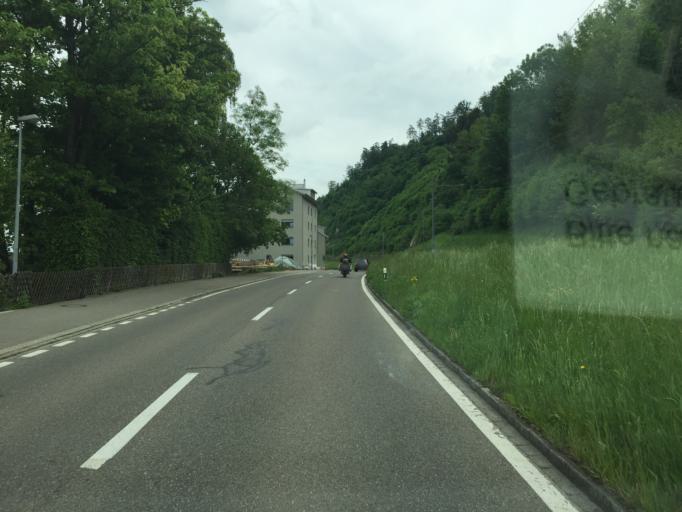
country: CH
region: Thurgau
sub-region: Frauenfeld District
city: Steckborn
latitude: 47.6710
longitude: 8.9997
